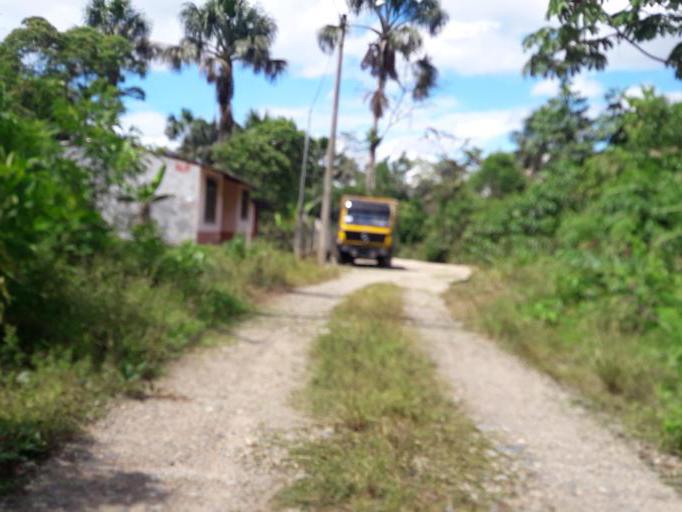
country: EC
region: Napo
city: Tena
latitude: -0.9566
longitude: -77.8197
